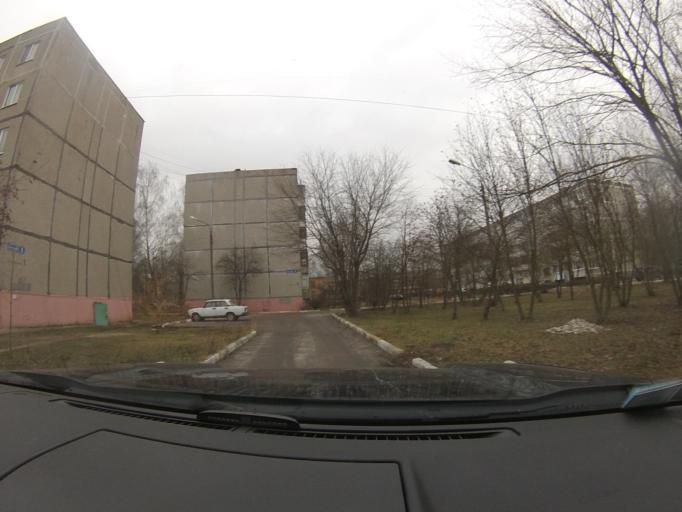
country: RU
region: Moskovskaya
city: Lopatinskiy
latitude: 55.3405
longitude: 38.7122
